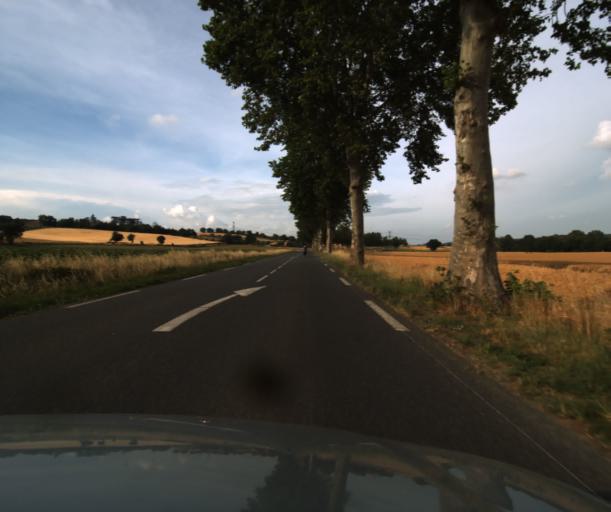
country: FR
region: Midi-Pyrenees
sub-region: Departement du Tarn-et-Garonne
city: Beaumont-de-Lomagne
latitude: 43.9167
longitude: 1.0563
